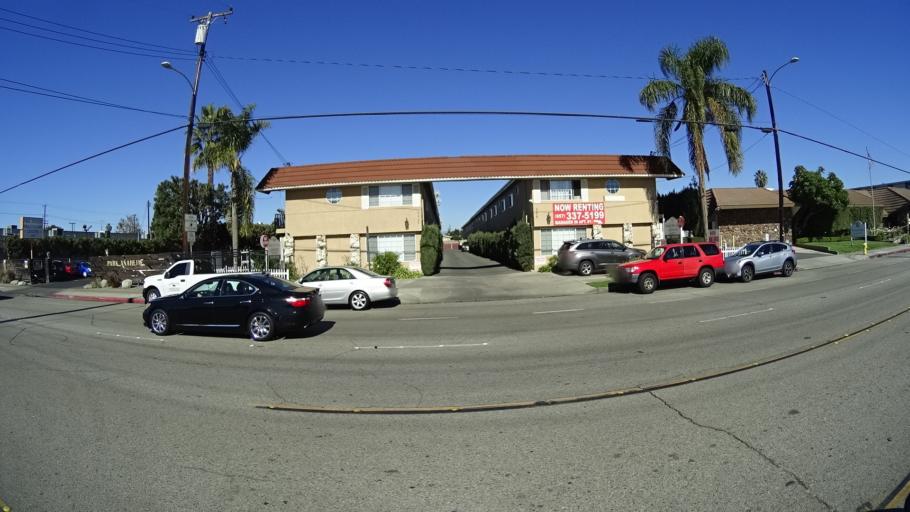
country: US
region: California
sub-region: Orange County
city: Stanton
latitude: 33.8176
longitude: -118.0096
